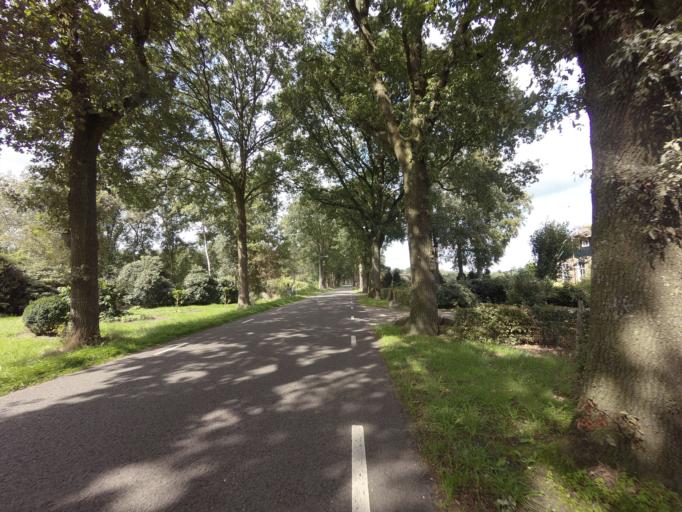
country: NL
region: Drenthe
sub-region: Gemeente De Wolden
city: Ruinen
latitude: 52.7130
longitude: 6.3368
